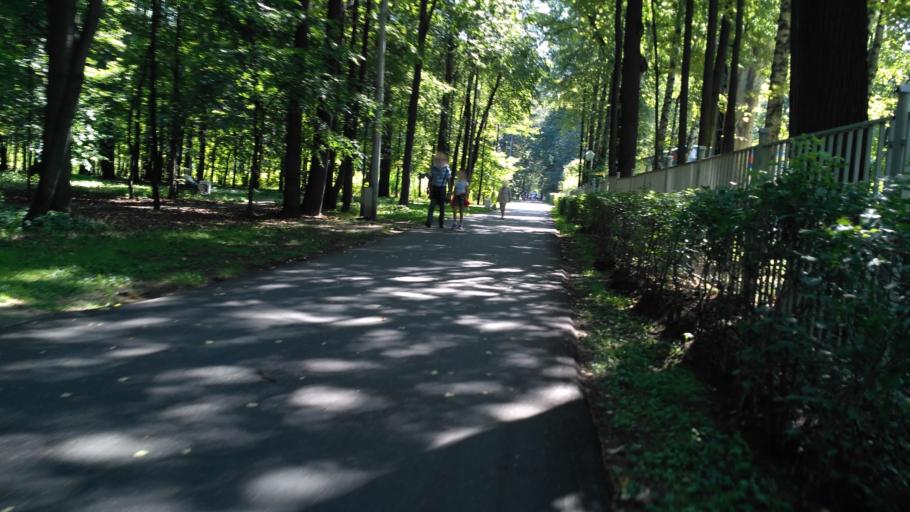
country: RU
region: Moscow
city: Metrogorodok
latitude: 55.7812
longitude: 37.7528
